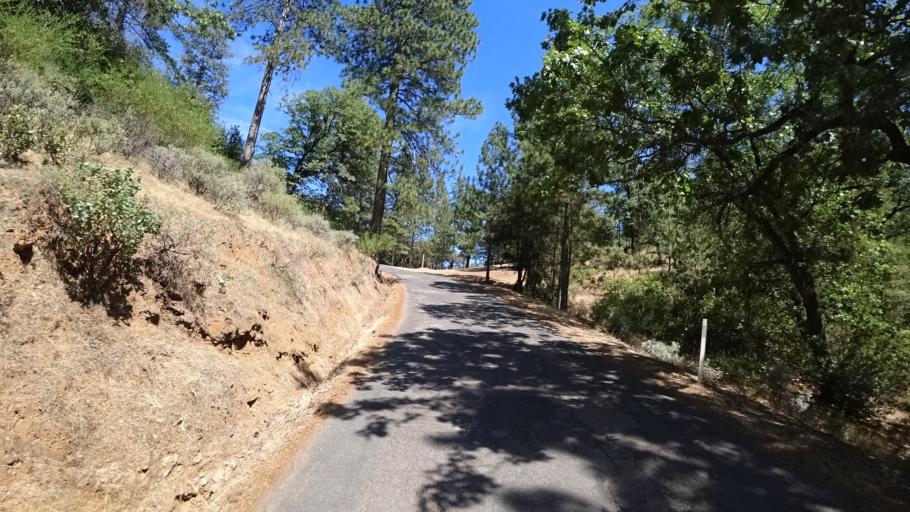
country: US
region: California
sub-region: Calaveras County
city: Murphys
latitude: 38.1696
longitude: -120.4693
